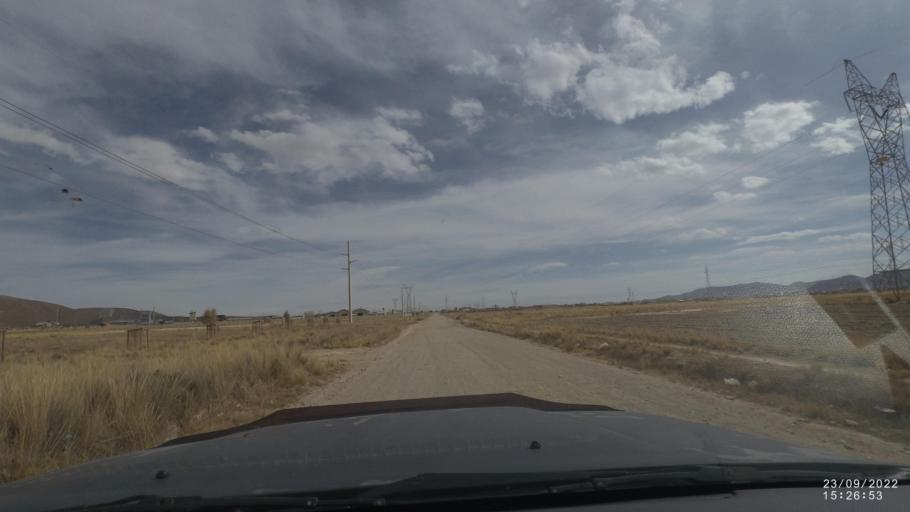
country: BO
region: Oruro
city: Oruro
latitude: -17.9573
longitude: -67.0412
